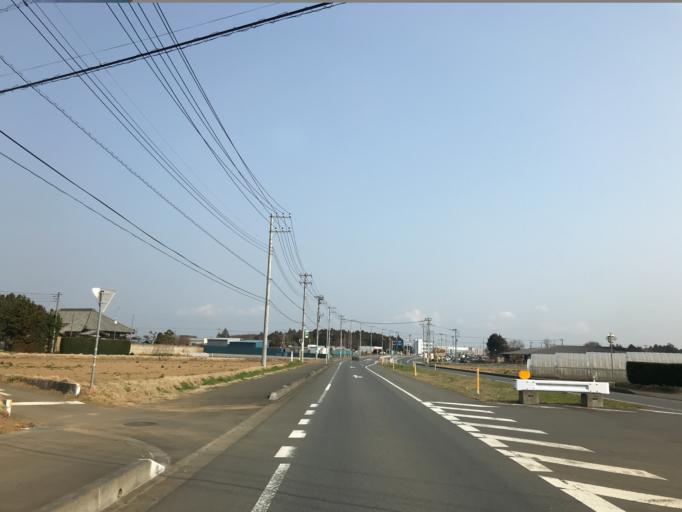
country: JP
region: Ibaraki
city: Okunoya
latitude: 36.1828
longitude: 140.3991
